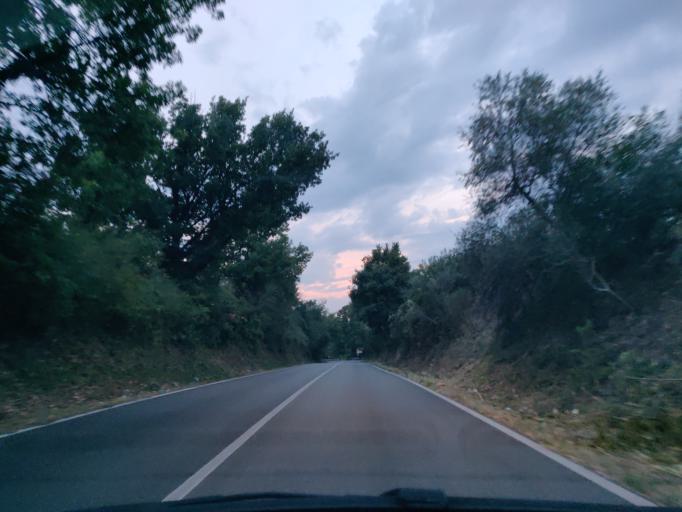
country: IT
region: Latium
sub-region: Provincia di Viterbo
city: San Martino al Cimino
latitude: 42.3844
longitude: 12.0816
